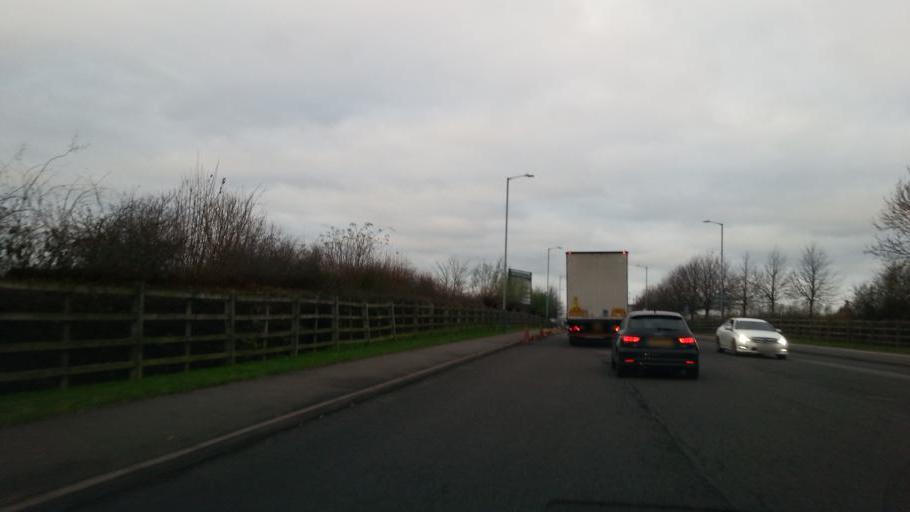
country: GB
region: England
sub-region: Coventry
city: Keresley
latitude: 52.4519
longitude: -1.5114
